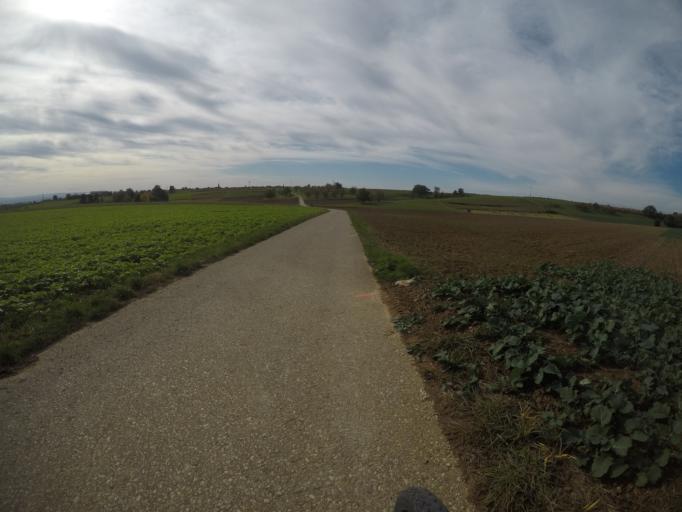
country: DE
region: Baden-Wuerttemberg
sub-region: Regierungsbezirk Stuttgart
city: Deckenpfronn
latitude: 48.6356
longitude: 8.8391
